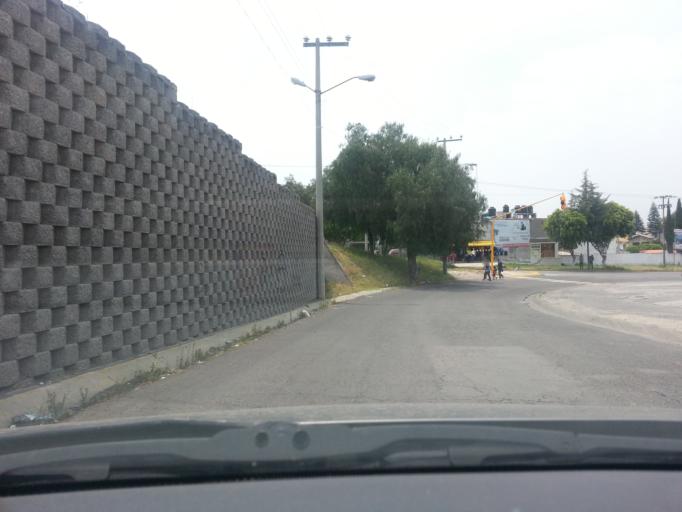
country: MX
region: Mexico
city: Cuautitlan Izcalli
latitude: 19.6590
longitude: -99.2097
